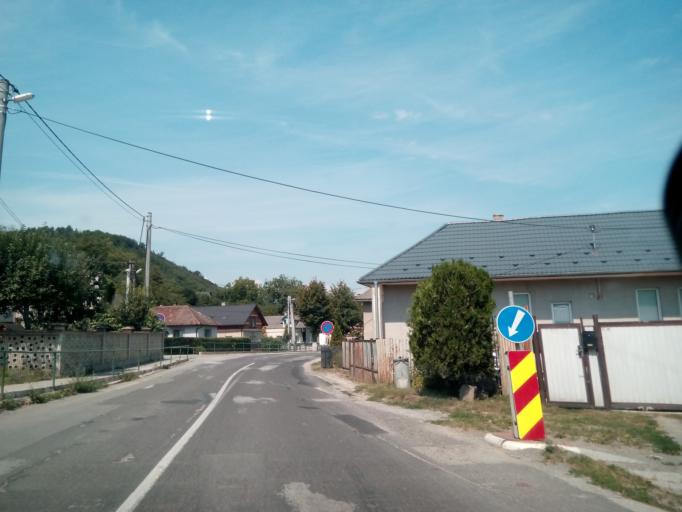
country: SK
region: Kosicky
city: Kosice
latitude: 48.7951
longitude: 21.2416
